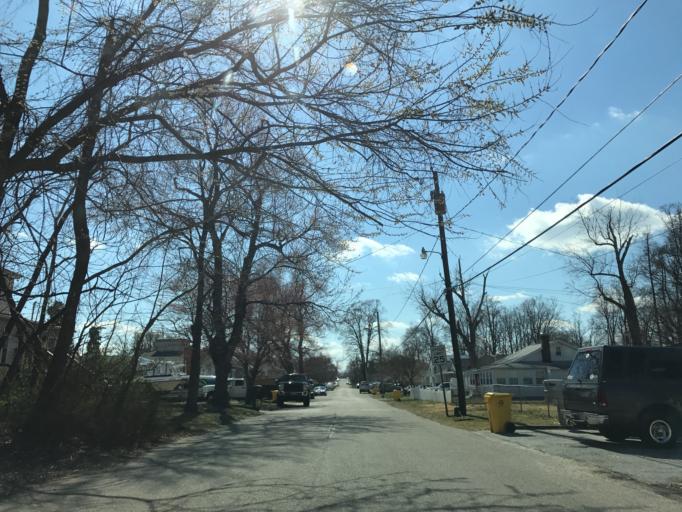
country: US
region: Maryland
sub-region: Anne Arundel County
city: Riviera Beach
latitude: 39.1649
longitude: -76.5038
